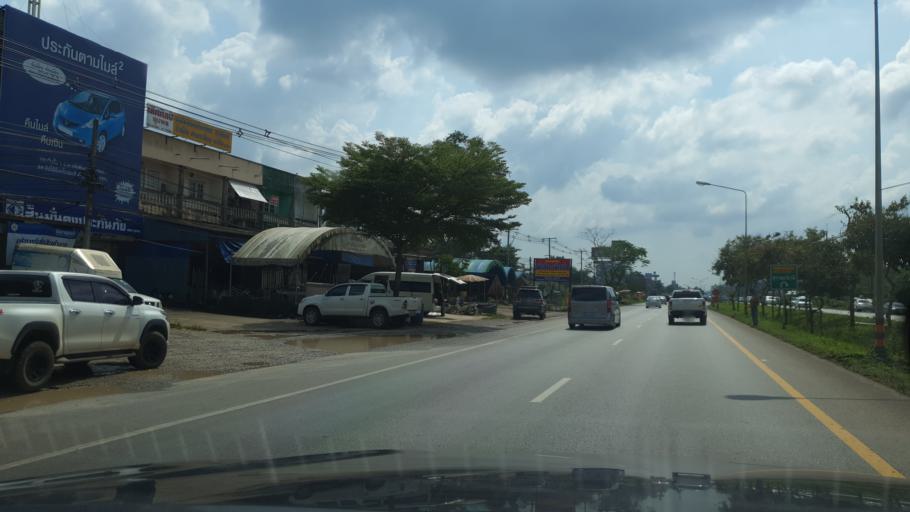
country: TH
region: Chumphon
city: Chumphon
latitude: 10.4996
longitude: 99.1195
